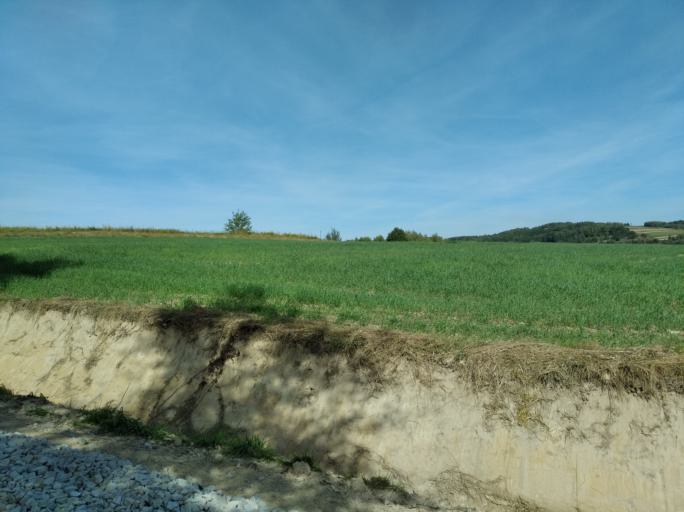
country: PL
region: Subcarpathian Voivodeship
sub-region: Powiat strzyzowski
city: Wisniowa
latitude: 49.9002
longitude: 21.6243
